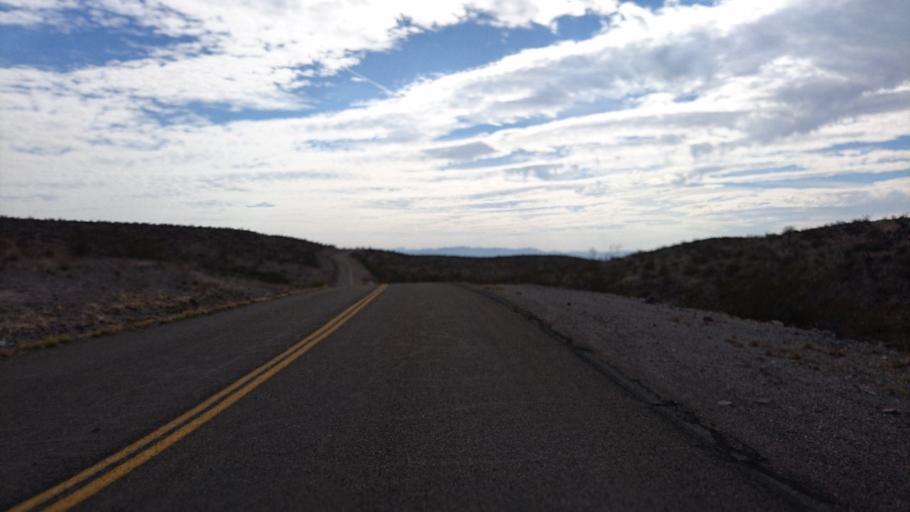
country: US
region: Arizona
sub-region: Mohave County
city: Mohave Valley
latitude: 34.8951
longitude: -114.4317
